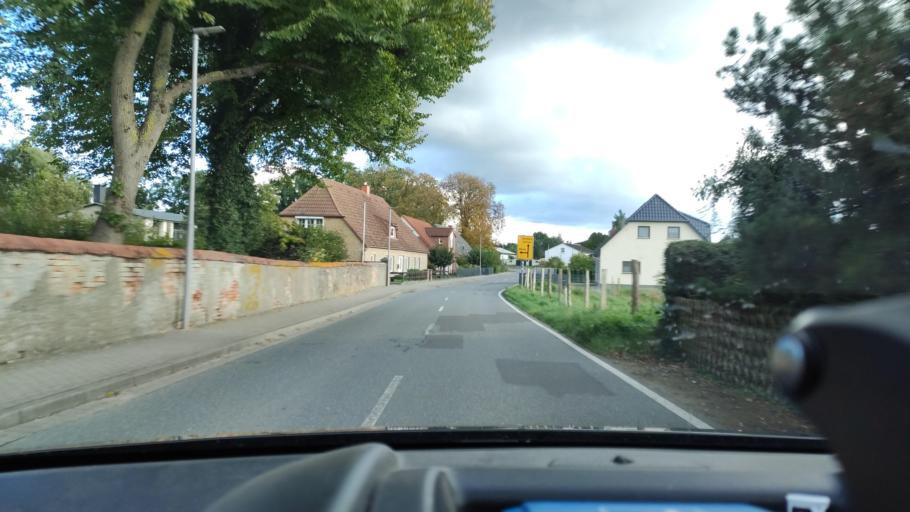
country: DE
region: Mecklenburg-Vorpommern
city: Butzow
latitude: 53.8220
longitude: 11.9371
